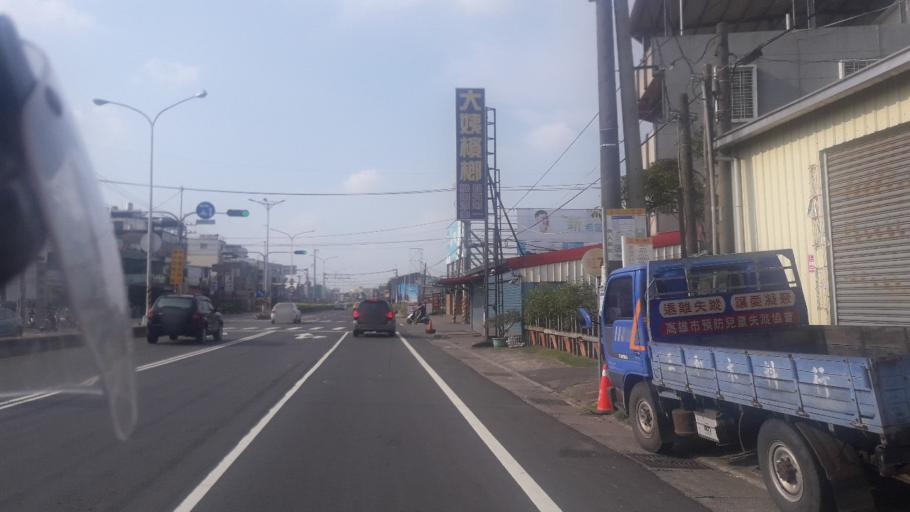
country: TW
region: Taiwan
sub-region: Tainan
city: Tainan
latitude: 22.8733
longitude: 120.2543
